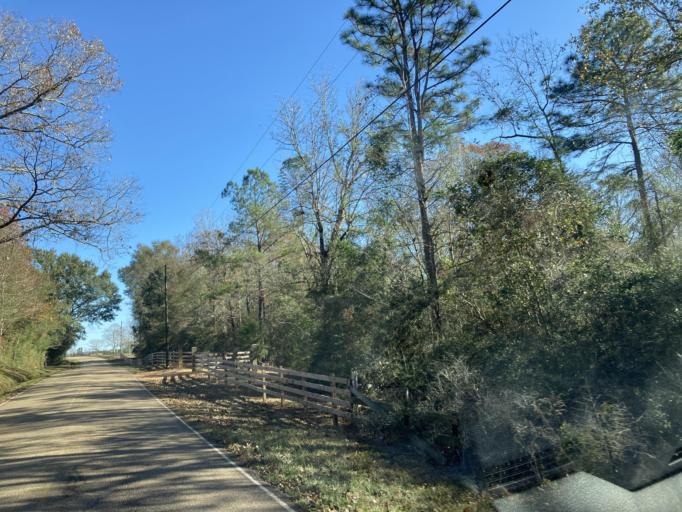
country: US
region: Mississippi
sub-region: Lamar County
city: Sumrall
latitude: 31.2685
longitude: -89.5286
